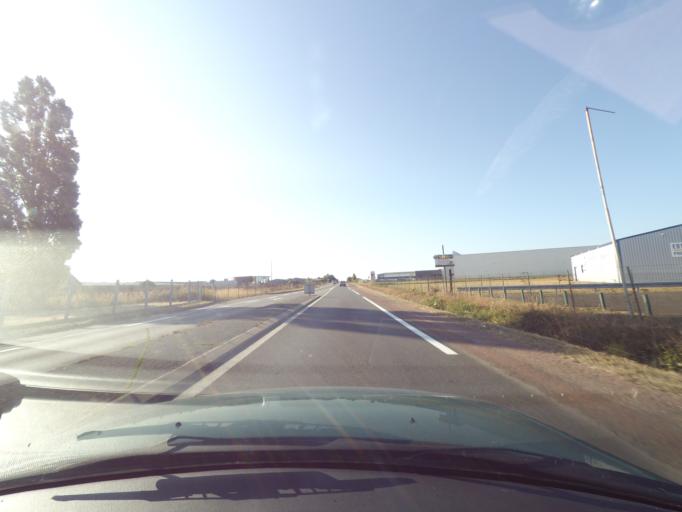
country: FR
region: Poitou-Charentes
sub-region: Departement des Deux-Sevres
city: Viennay
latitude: 46.6694
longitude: -0.2553
